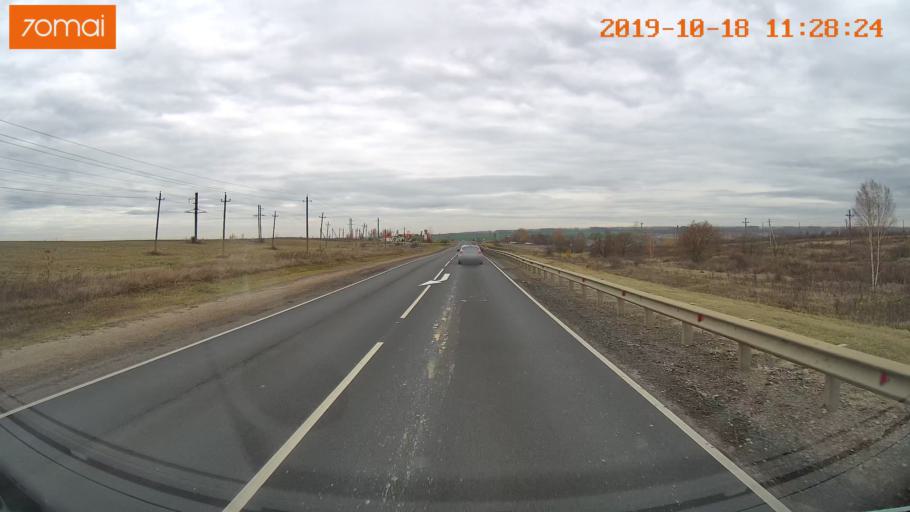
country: RU
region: Tula
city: Kimovsk
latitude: 54.1539
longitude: 38.6602
